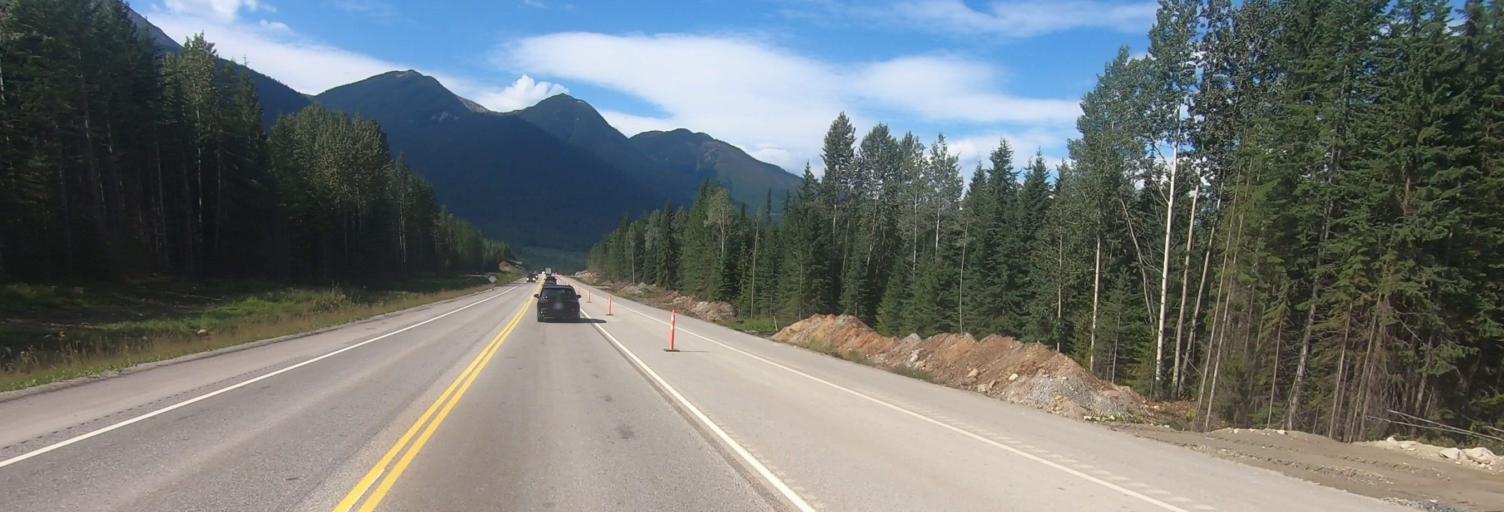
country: CA
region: British Columbia
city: Golden
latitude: 51.4824
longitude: -117.3402
